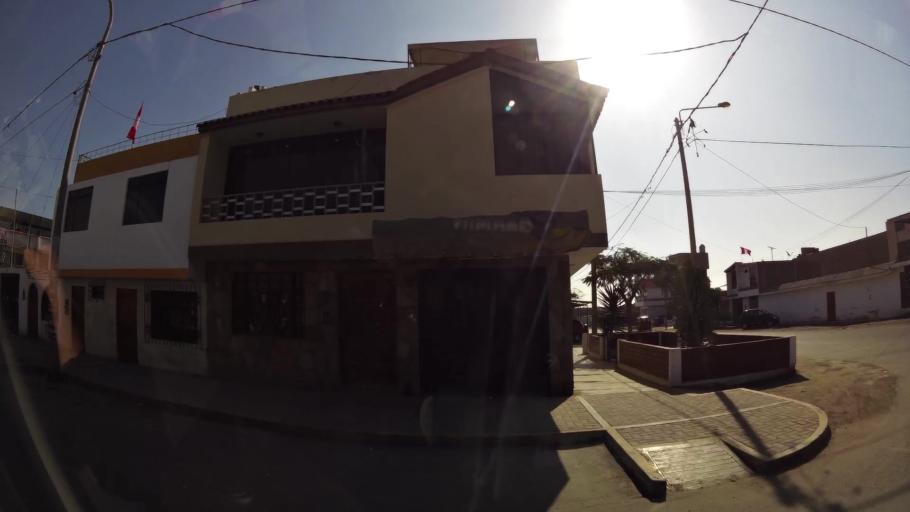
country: PE
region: Ica
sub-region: Provincia de Chincha
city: Chincha Alta
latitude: -13.4082
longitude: -76.1308
